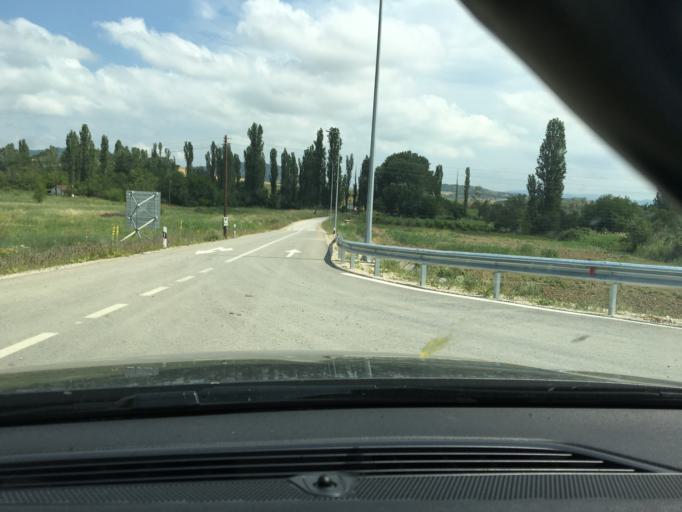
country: MK
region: Sveti Nikole
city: Gorobinci
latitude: 41.9179
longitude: 21.8792
